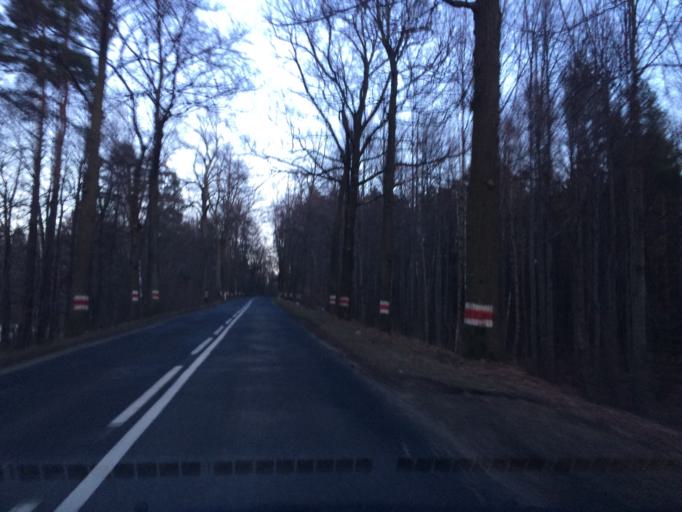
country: PL
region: Lower Silesian Voivodeship
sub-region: Powiat lwowecki
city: Wlen
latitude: 51.1194
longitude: 15.7085
